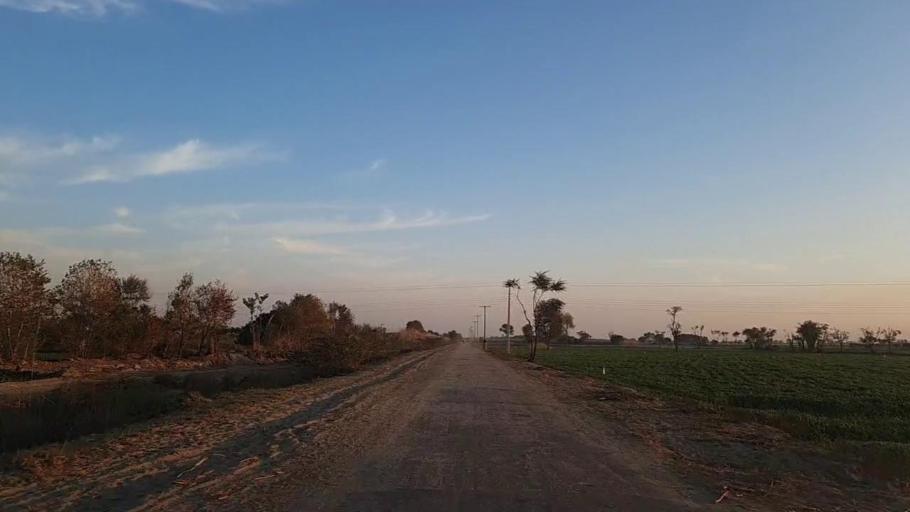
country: PK
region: Sindh
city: Bandhi
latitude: 26.6252
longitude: 68.3716
